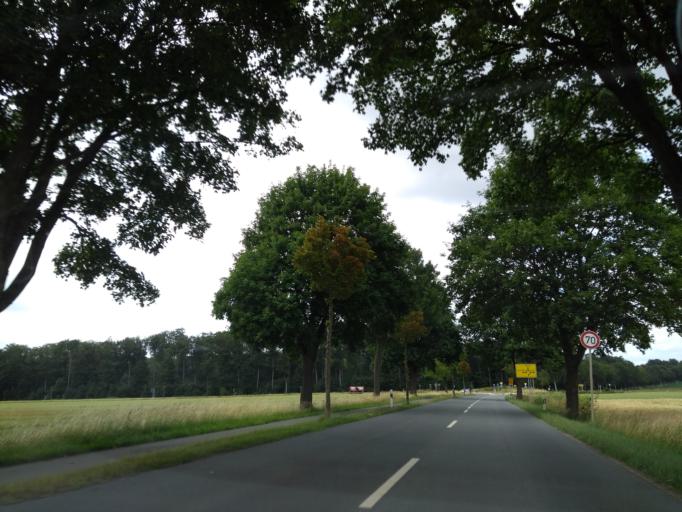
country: DE
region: North Rhine-Westphalia
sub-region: Regierungsbezirk Detmold
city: Salzkotten
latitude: 51.6569
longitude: 8.6714
